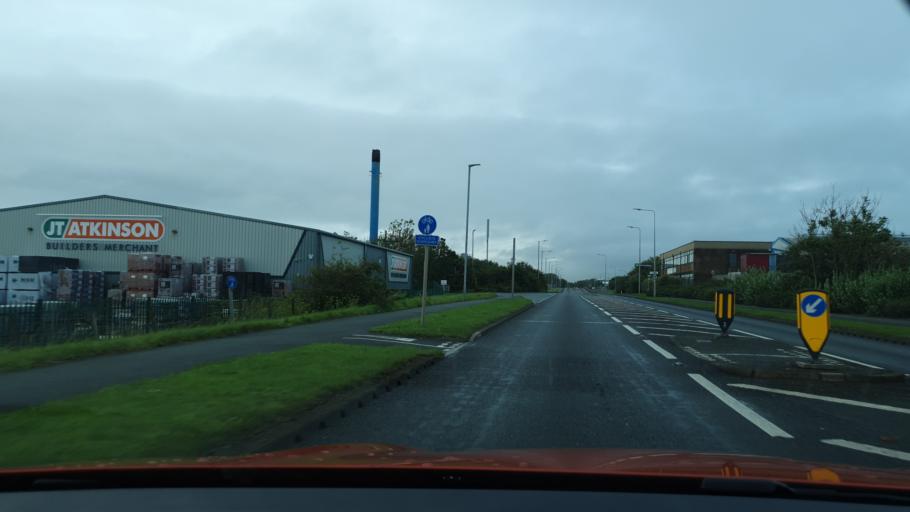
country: GB
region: England
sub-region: Cumbria
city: Barrow in Furness
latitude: 54.1401
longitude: -3.2327
